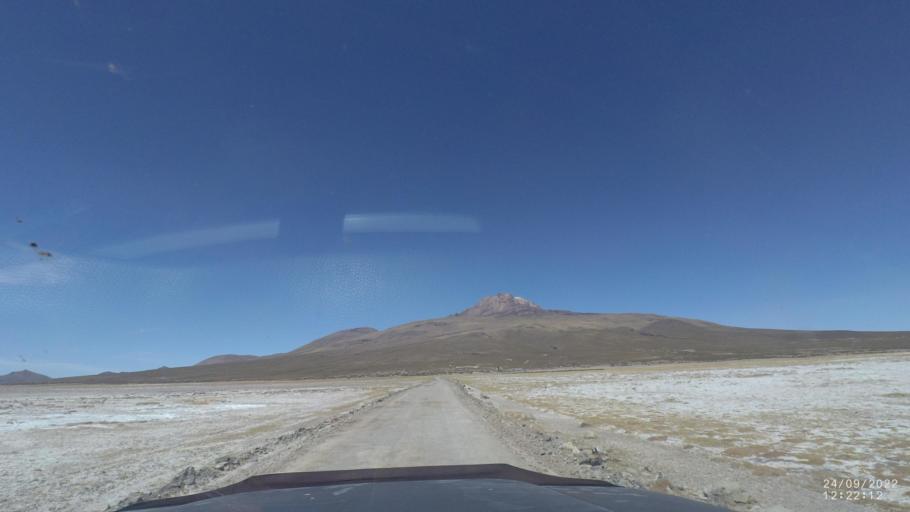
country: BO
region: Potosi
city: Colchani
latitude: -19.7545
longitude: -67.6661
